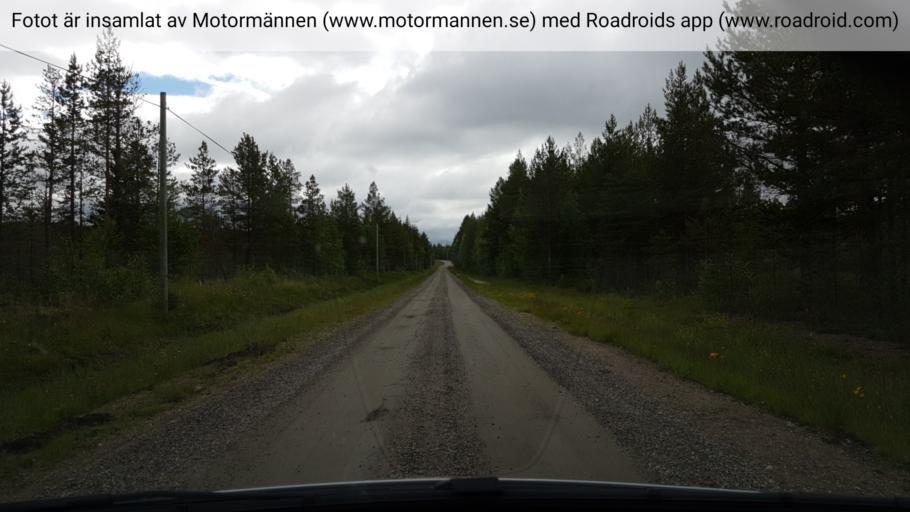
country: SE
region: Vaesterbotten
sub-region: Lycksele Kommun
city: Lycksele
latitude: 64.5628
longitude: 19.0012
